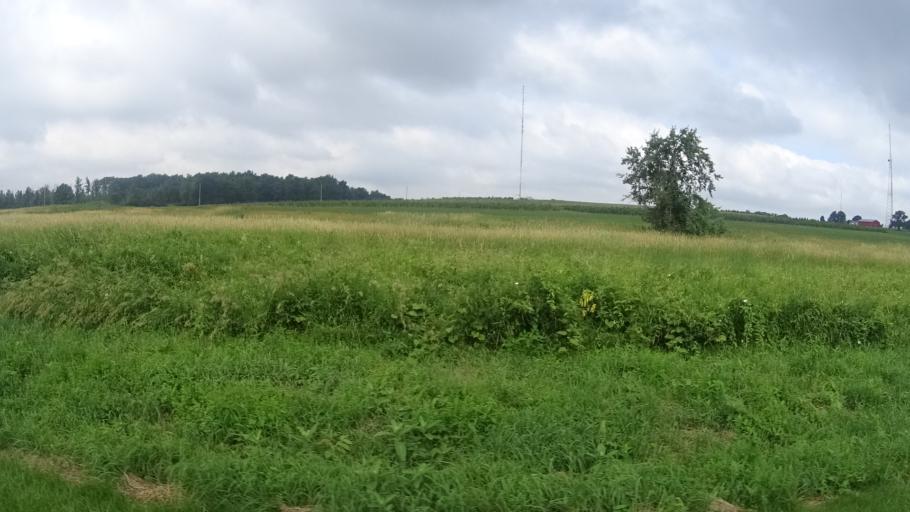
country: US
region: Ohio
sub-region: Huron County
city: Wakeman
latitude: 41.3014
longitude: -82.4811
